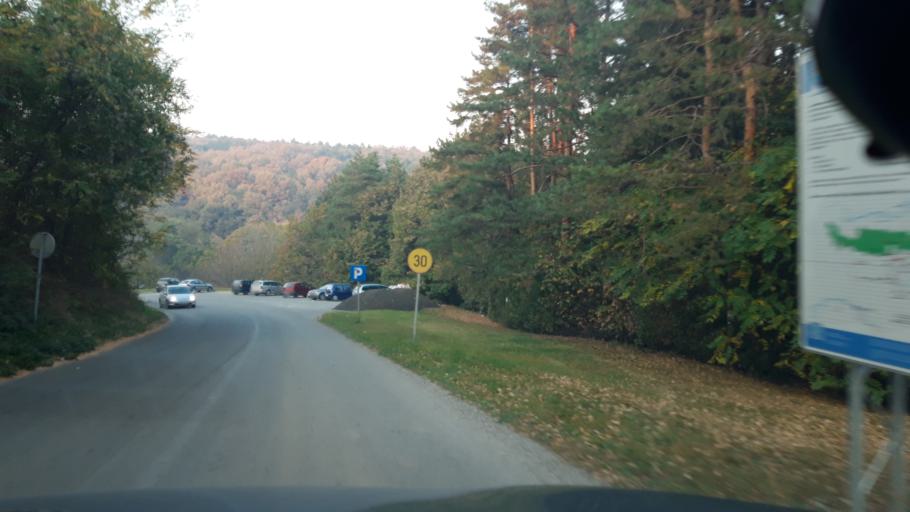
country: RS
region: Autonomna Pokrajina Vojvodina
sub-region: Sremski Okrug
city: Irig
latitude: 45.1266
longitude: 19.8467
